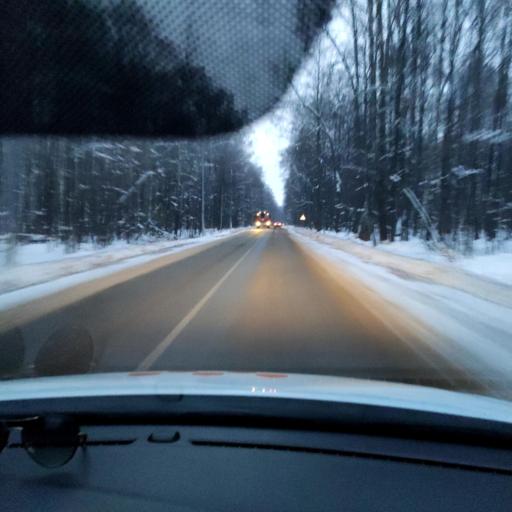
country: RU
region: Tatarstan
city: Vysokaya Gora
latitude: 55.9319
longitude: 49.1658
